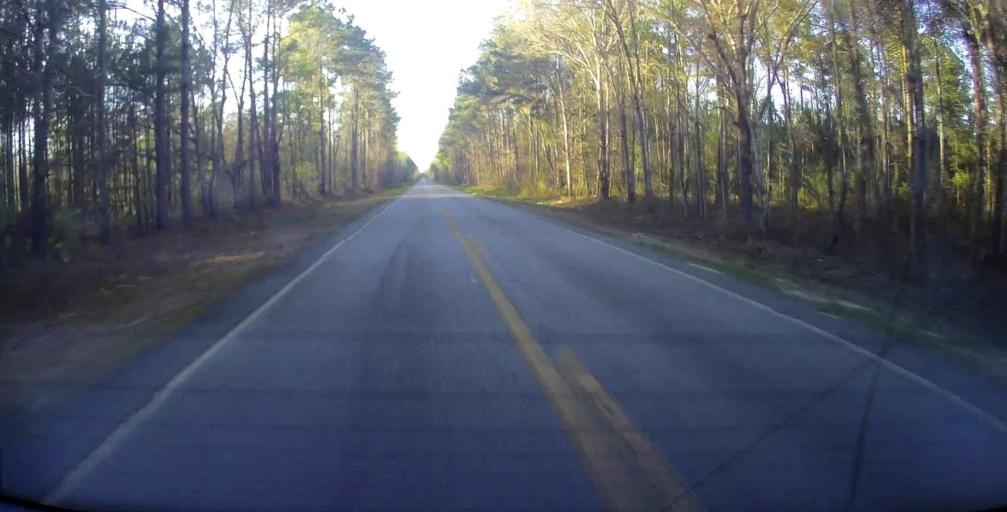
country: US
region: Georgia
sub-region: Wilcox County
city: Abbeville
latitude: 32.0896
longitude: -83.2945
